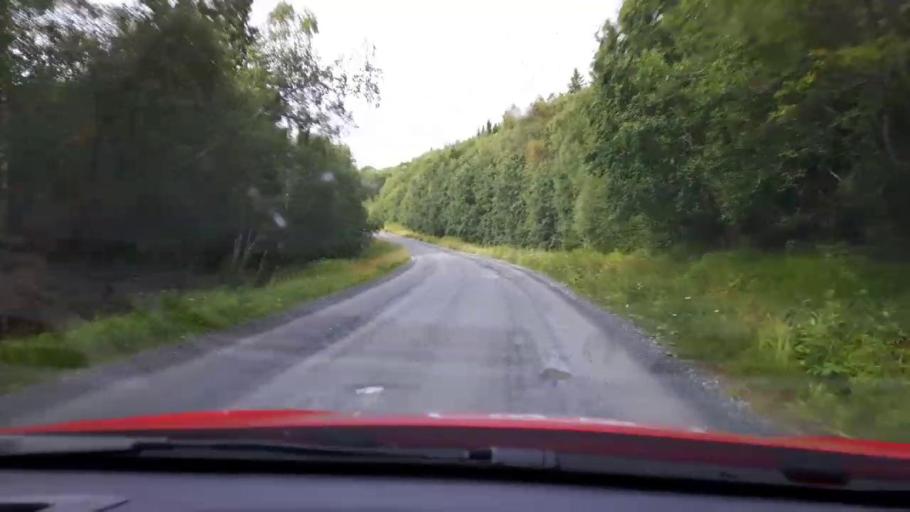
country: SE
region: Jaemtland
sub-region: Are Kommun
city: Are
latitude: 63.7389
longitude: 13.0166
